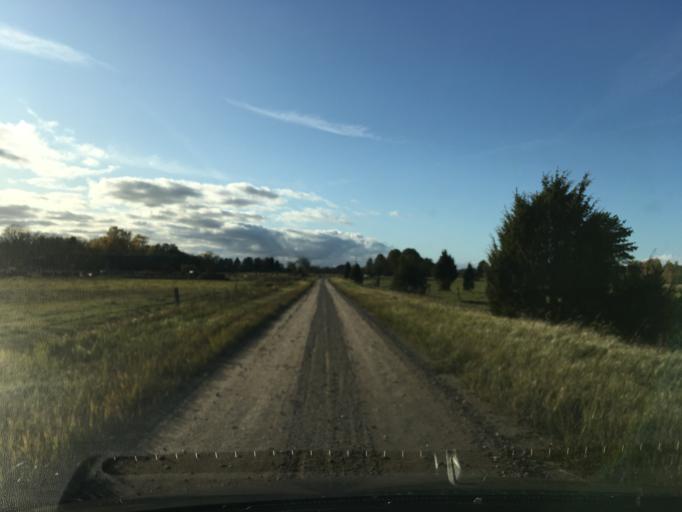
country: EE
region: Laeaene
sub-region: Lihula vald
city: Lihula
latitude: 58.5636
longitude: 23.8040
